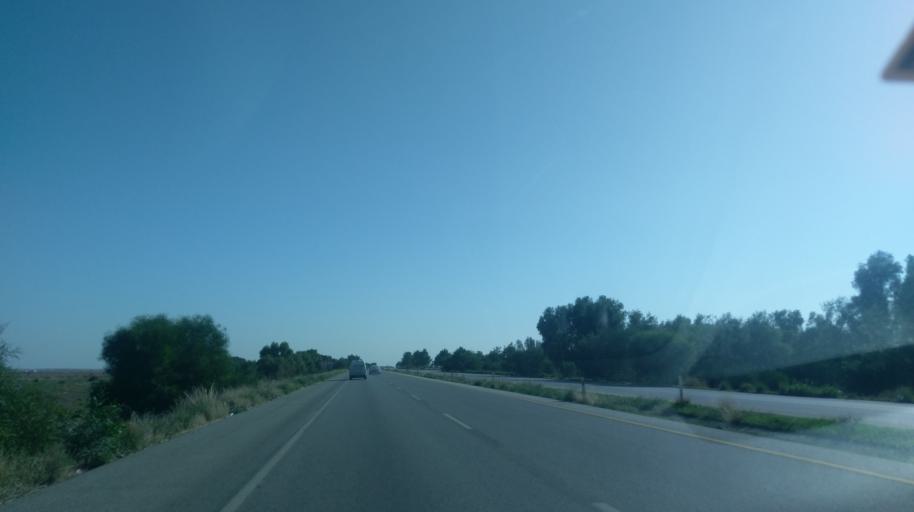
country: CY
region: Ammochostos
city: Lefkonoiko
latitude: 35.1861
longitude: 33.6560
